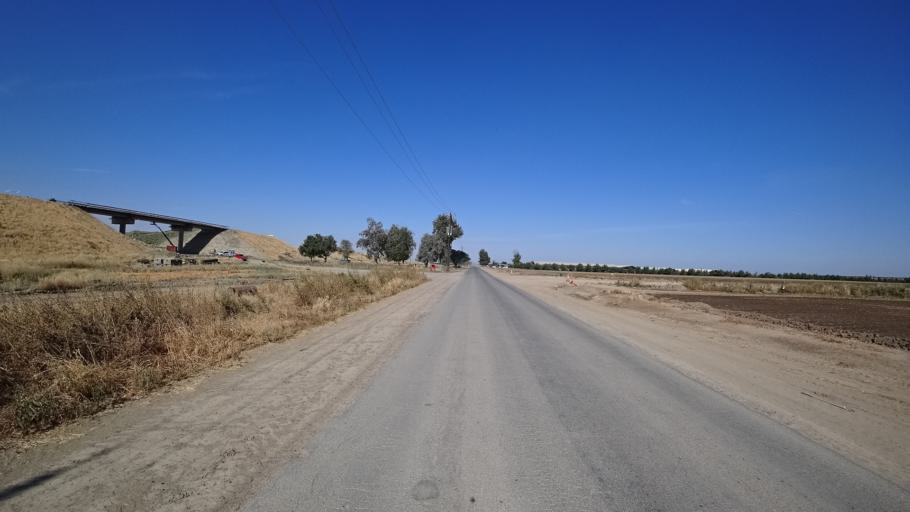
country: US
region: California
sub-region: Kings County
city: Home Garden
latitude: 36.2259
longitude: -119.6056
